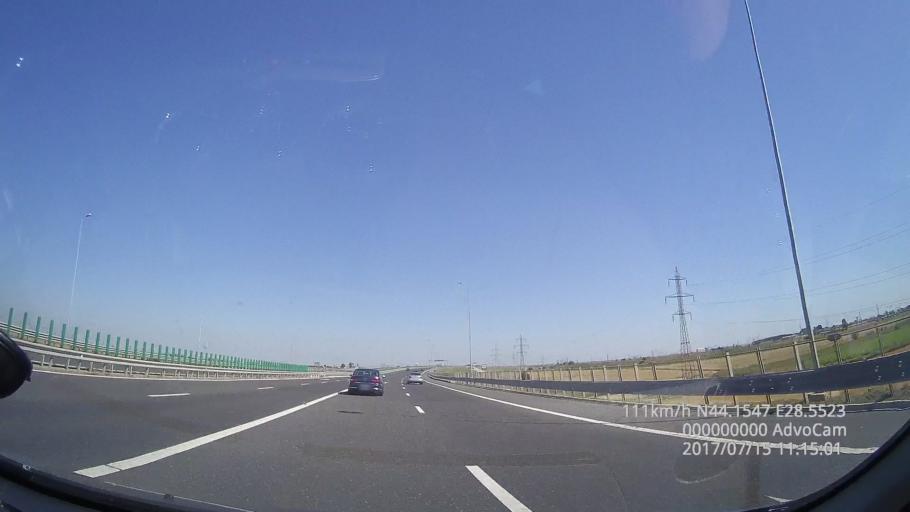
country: RO
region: Constanta
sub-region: Comuna Cumpana
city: Cumpana
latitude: 44.1557
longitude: 28.5518
